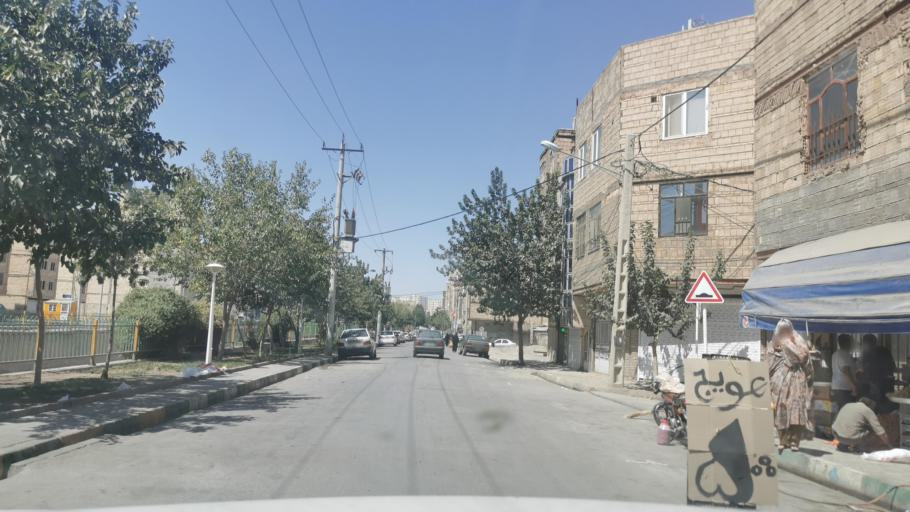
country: IR
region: Razavi Khorasan
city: Mashhad
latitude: 36.3595
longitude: 59.5612
